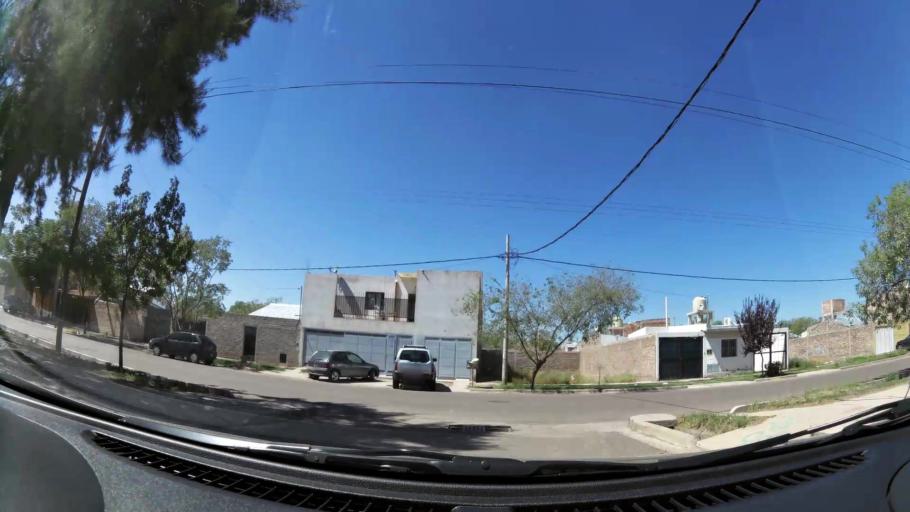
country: AR
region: Mendoza
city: Las Heras
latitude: -32.8429
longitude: -68.8489
